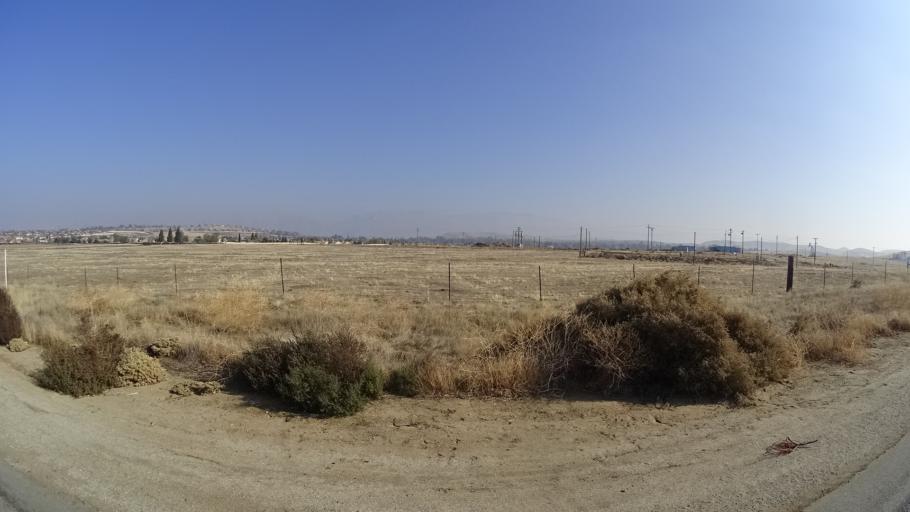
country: US
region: California
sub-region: Kern County
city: Lamont
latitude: 35.4030
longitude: -118.8588
